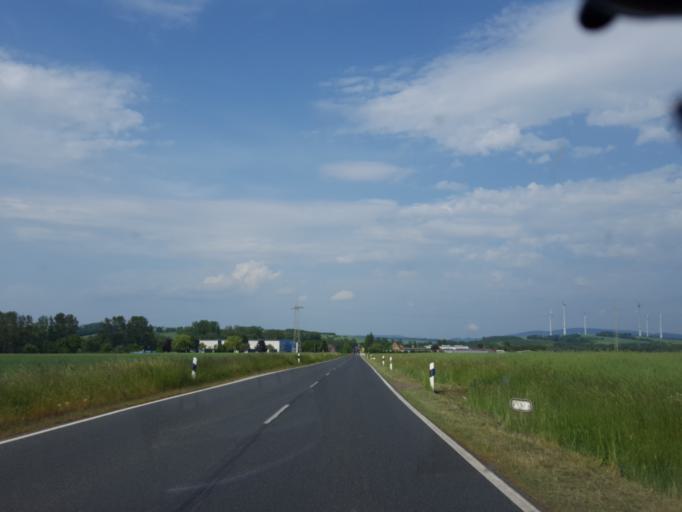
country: DE
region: Lower Saxony
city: Wulften
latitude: 51.6496
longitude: 10.1648
